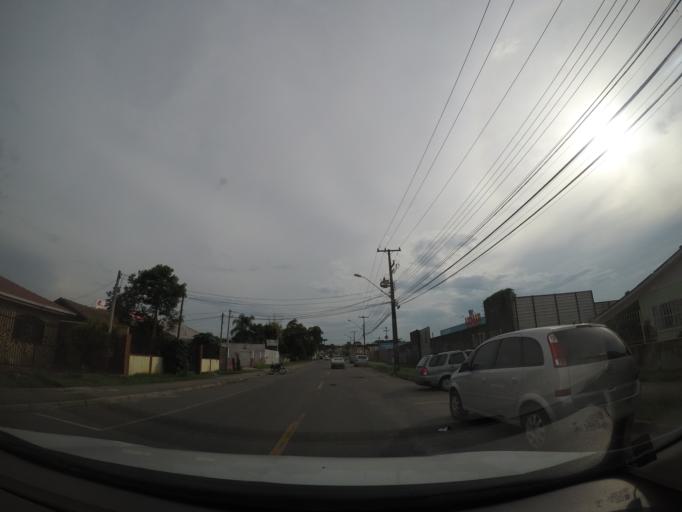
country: BR
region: Parana
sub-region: Sao Jose Dos Pinhais
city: Sao Jose dos Pinhais
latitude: -25.5050
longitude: -49.2307
